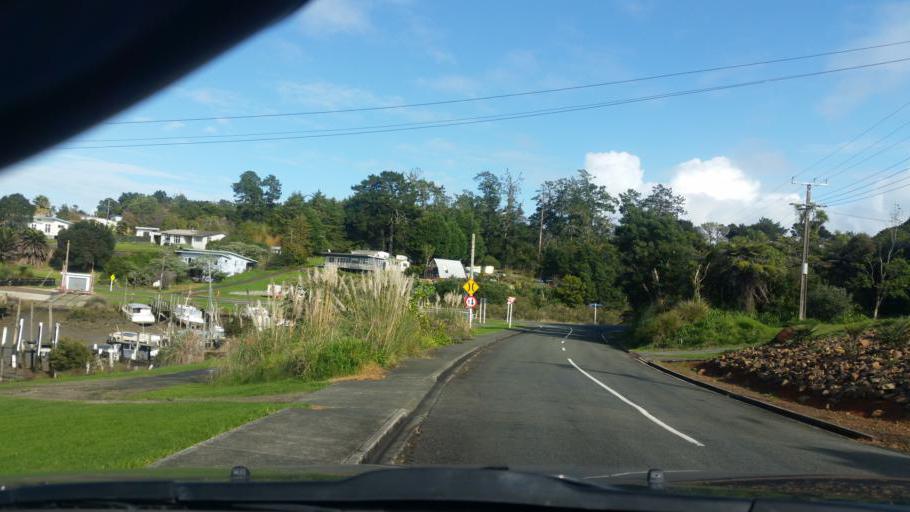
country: NZ
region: Auckland
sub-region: Auckland
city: Wellsford
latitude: -36.2477
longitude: 174.2474
